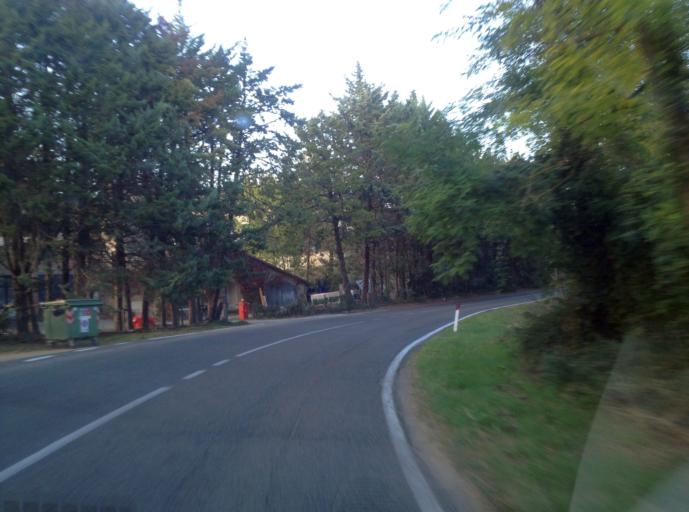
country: IT
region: Tuscany
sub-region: Provincia di Siena
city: Castellina in Chianti
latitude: 43.4518
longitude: 11.2923
